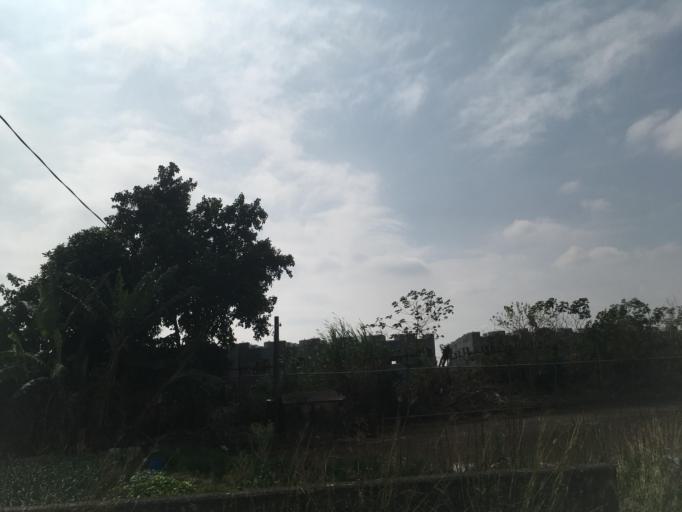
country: TW
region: Taiwan
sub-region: Yunlin
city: Douliu
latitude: 23.6931
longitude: 120.4591
